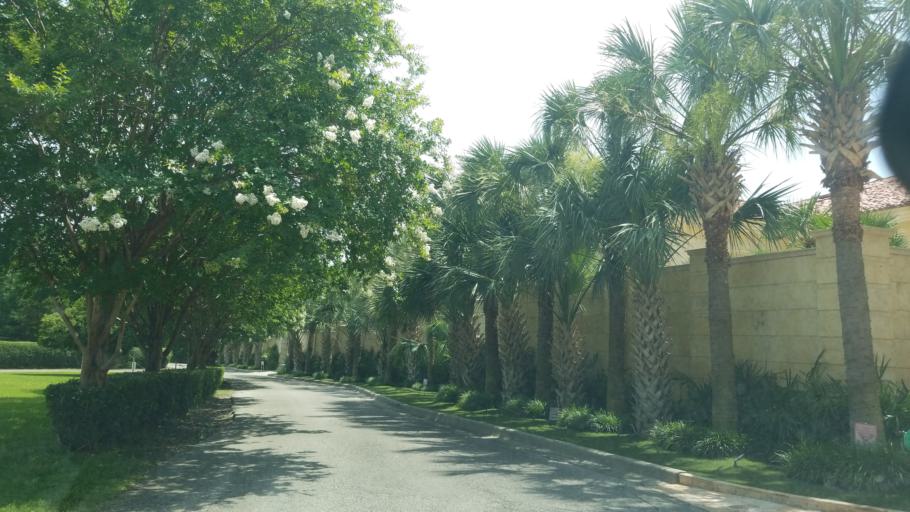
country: US
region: Texas
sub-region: Dallas County
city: University Park
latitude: 32.8696
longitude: -96.8072
